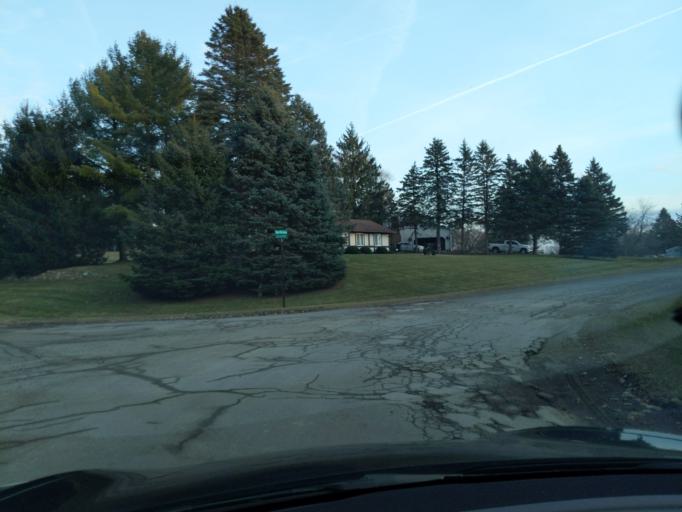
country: US
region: Michigan
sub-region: Livingston County
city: Brighton
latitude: 42.6449
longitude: -83.7228
